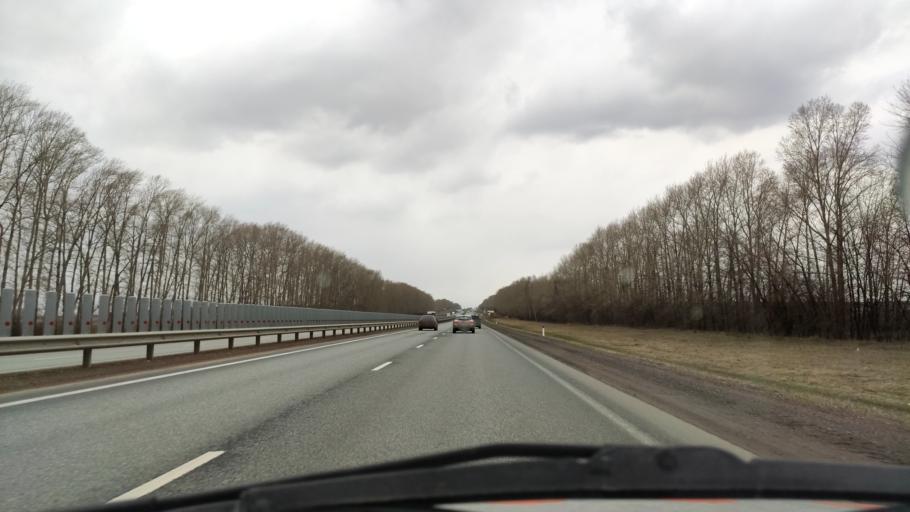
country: RU
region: Bashkortostan
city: Asanovo
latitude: 55.0192
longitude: 55.4753
